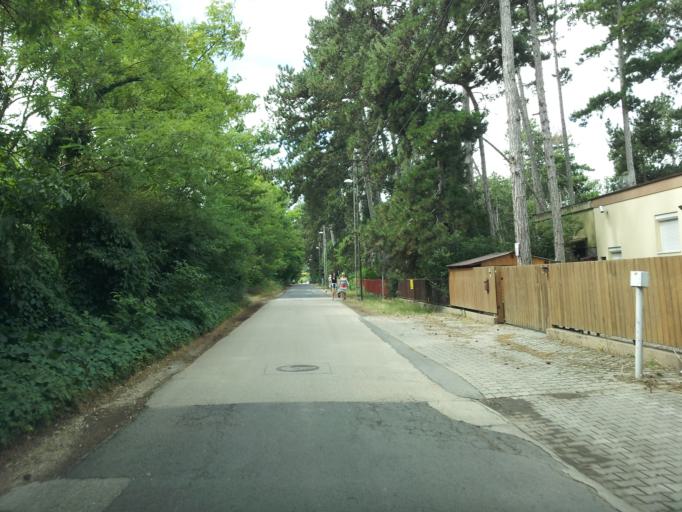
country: HU
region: Somogy
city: Balatonszabadi
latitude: 46.9426
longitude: 18.1337
